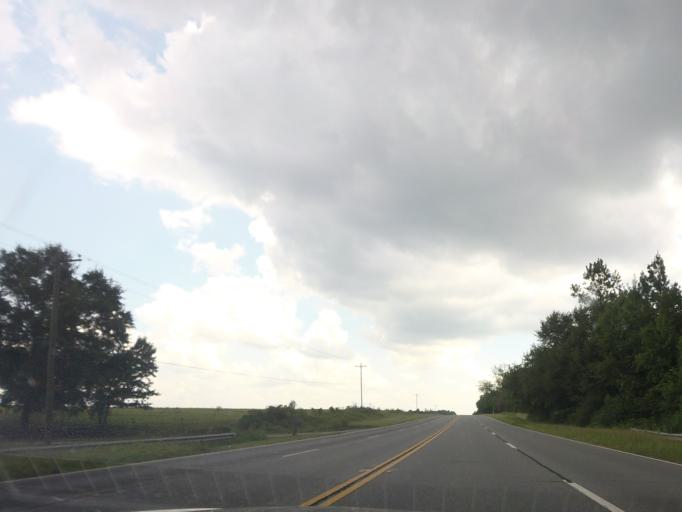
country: US
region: Georgia
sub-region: Bleckley County
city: Cochran
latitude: 32.4289
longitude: -83.3674
